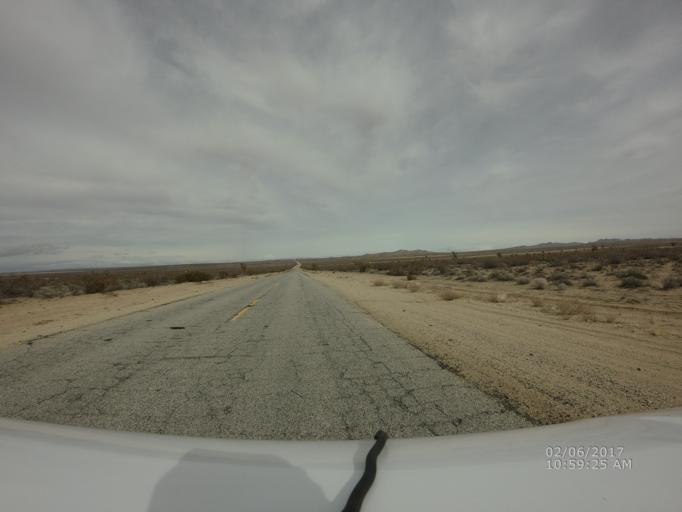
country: US
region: California
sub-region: Los Angeles County
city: Lake Los Angeles
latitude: 34.6380
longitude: -117.7026
